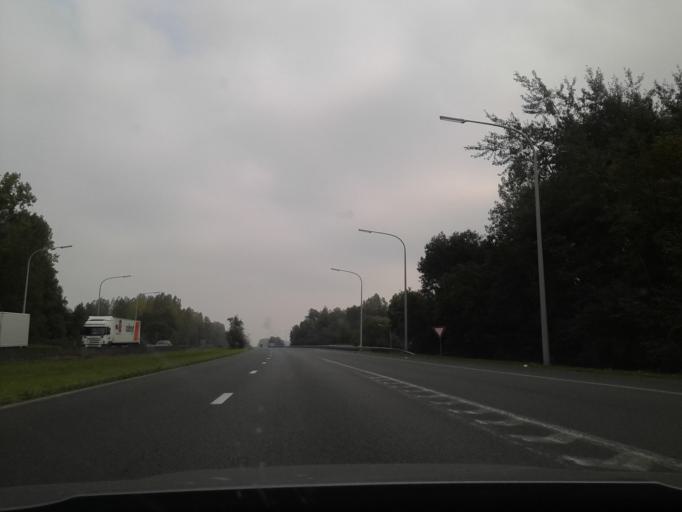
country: BE
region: Wallonia
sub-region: Province du Hainaut
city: Tournai
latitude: 50.6351
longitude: 3.4213
